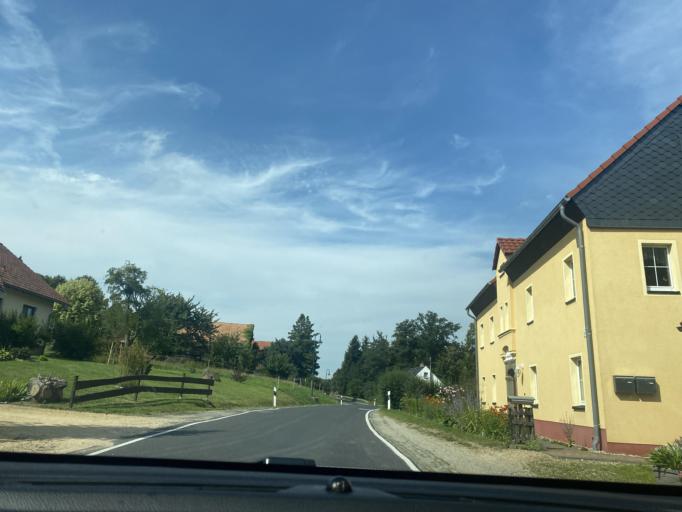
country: DE
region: Saxony
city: Sohland am Rotstein
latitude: 51.1097
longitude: 14.7827
